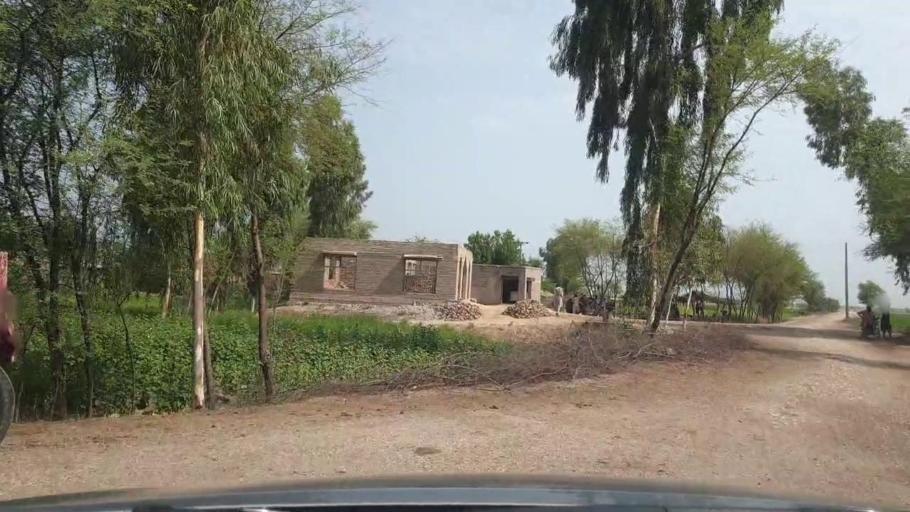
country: PK
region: Sindh
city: Rohri
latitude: 27.6577
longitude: 69.0243
